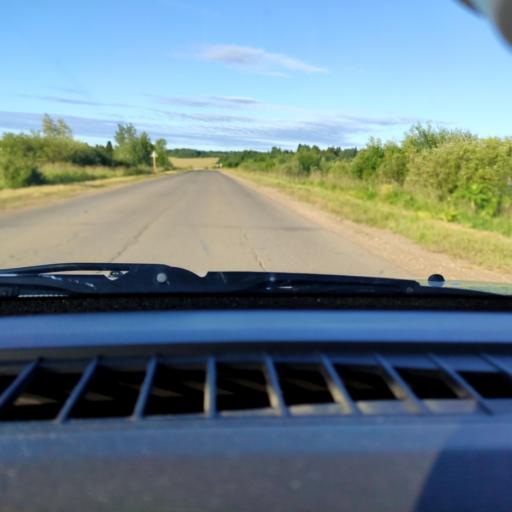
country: RU
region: Perm
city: Uinskoye
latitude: 57.0846
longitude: 56.5570
